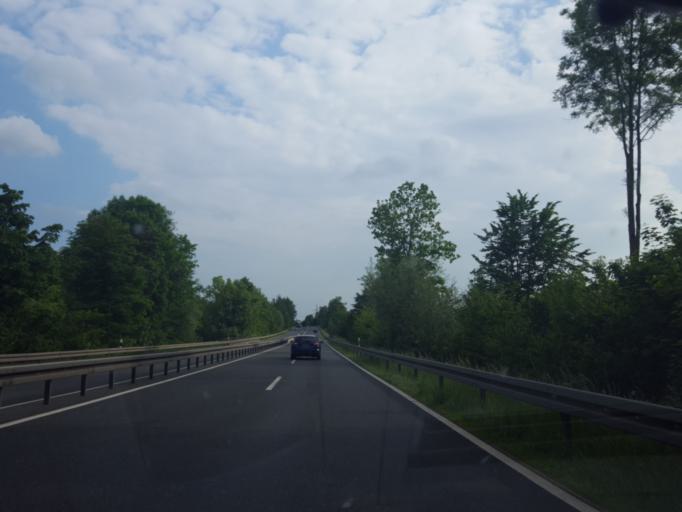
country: DE
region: Lower Saxony
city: Gittelde
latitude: 51.8168
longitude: 10.1891
